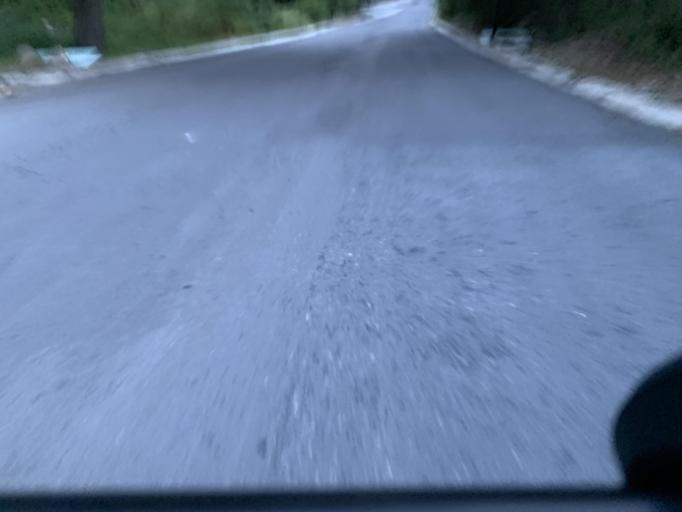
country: MX
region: Nuevo Leon
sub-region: Juarez
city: Bosques de San Pedro
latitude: 25.5191
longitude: -100.1832
